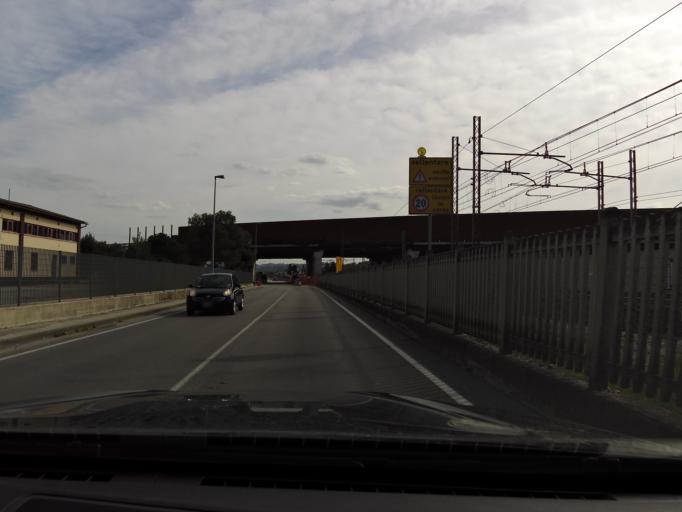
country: IT
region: The Marches
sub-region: Provincia di Ancona
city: San Biagio
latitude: 43.5271
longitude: 13.5217
